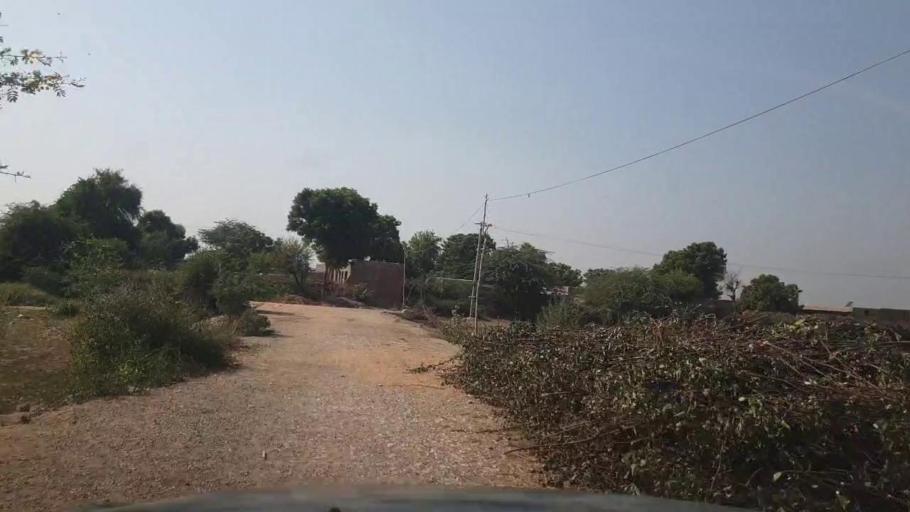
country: PK
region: Sindh
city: Bhit Shah
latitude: 25.7299
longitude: 68.4953
